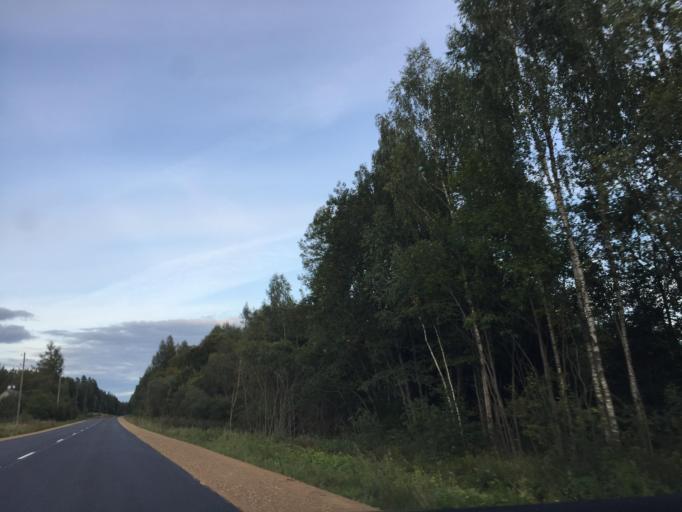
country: LV
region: Viesite
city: Viesite
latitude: 56.3932
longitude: 25.6840
